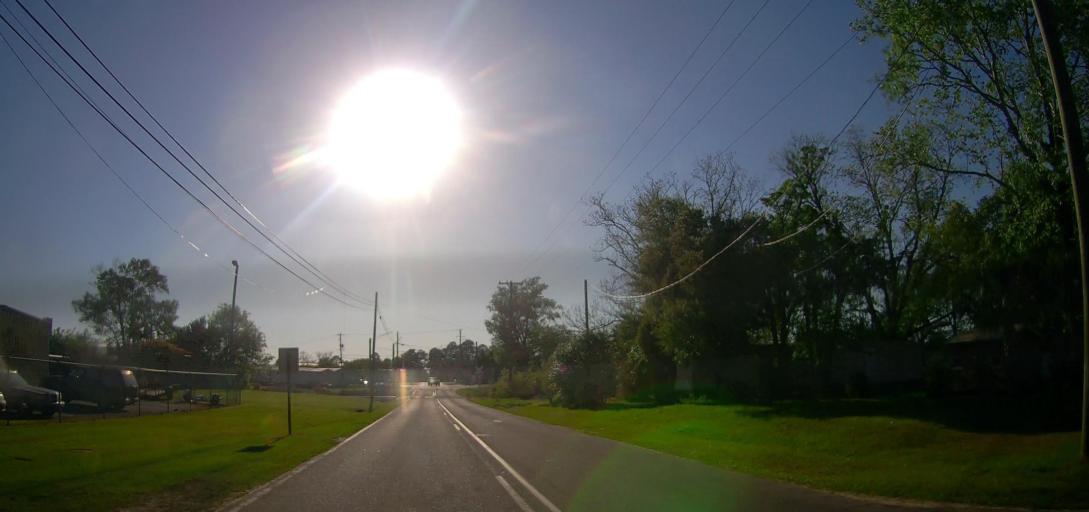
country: US
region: Georgia
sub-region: Ben Hill County
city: Fitzgerald
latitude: 31.7059
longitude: -83.2503
